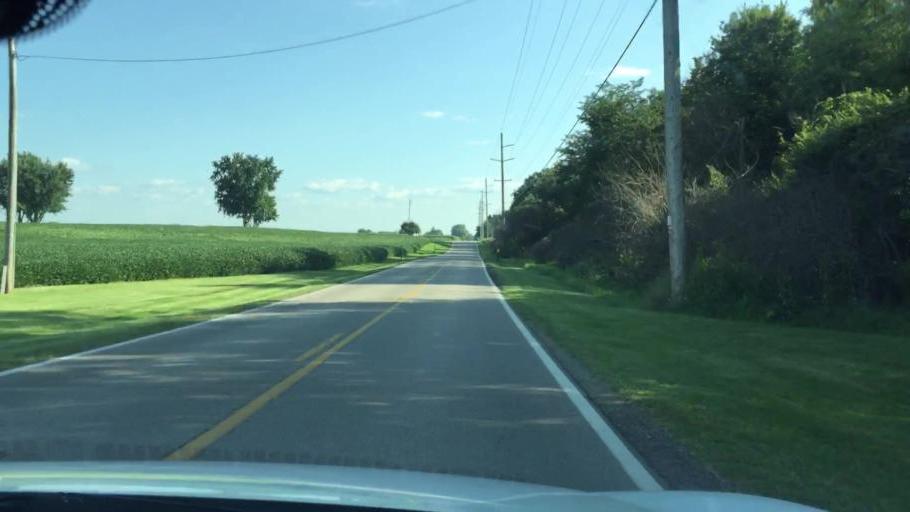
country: US
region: Ohio
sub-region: Clark County
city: Northridge
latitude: 39.9493
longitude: -83.7095
